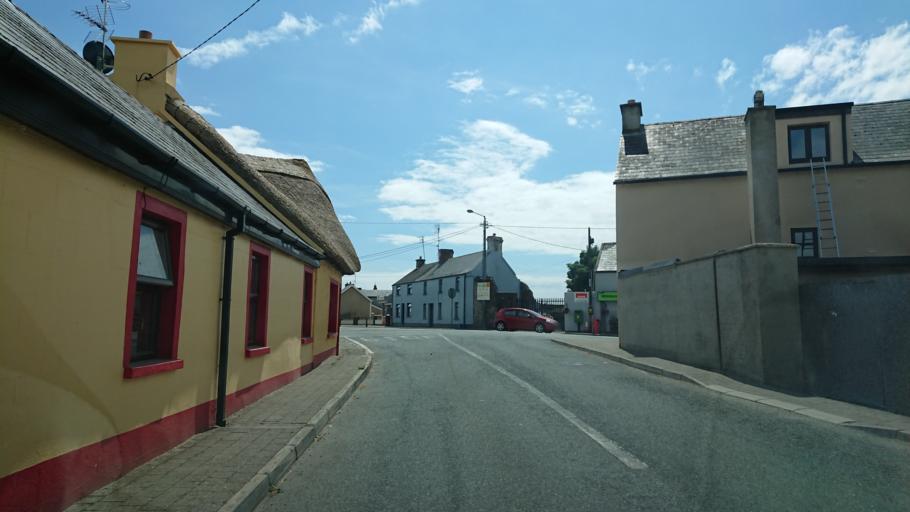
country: IE
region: Munster
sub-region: Waterford
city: Portlaw
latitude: 52.1769
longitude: -7.3354
